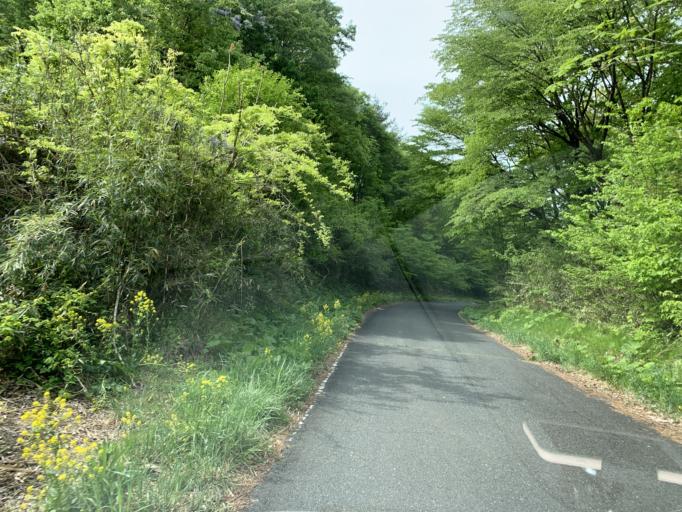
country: JP
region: Iwate
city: Ichinoseki
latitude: 38.8679
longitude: 141.0657
